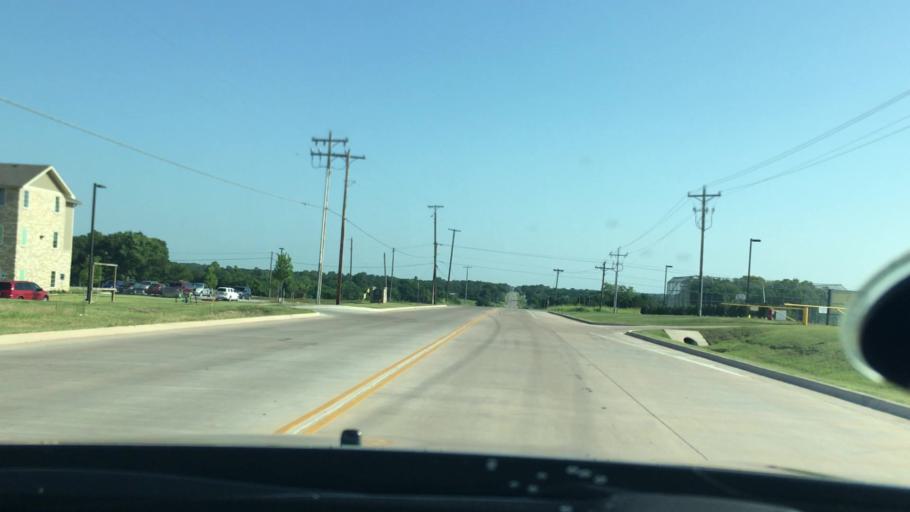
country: US
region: Oklahoma
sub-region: Pontotoc County
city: Ada
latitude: 34.7949
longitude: -96.6523
